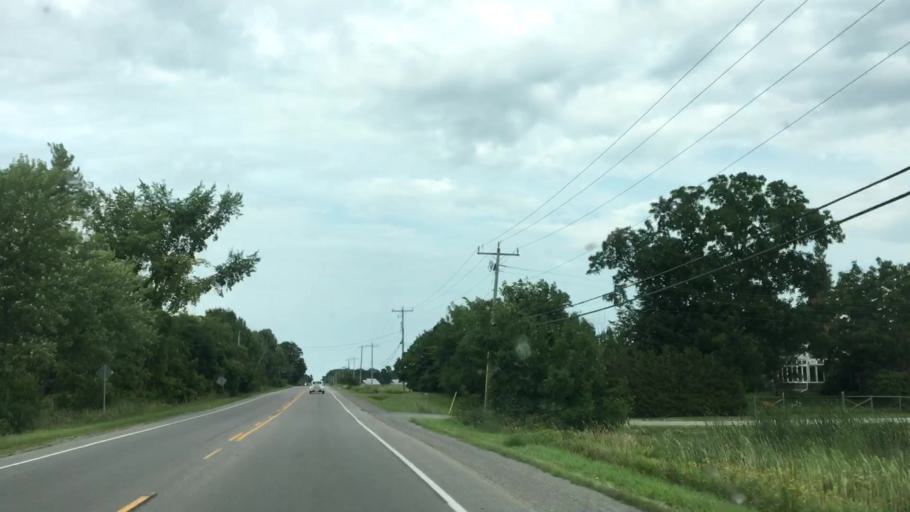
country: CA
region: Ontario
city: Quinte West
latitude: 44.0874
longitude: -77.6325
